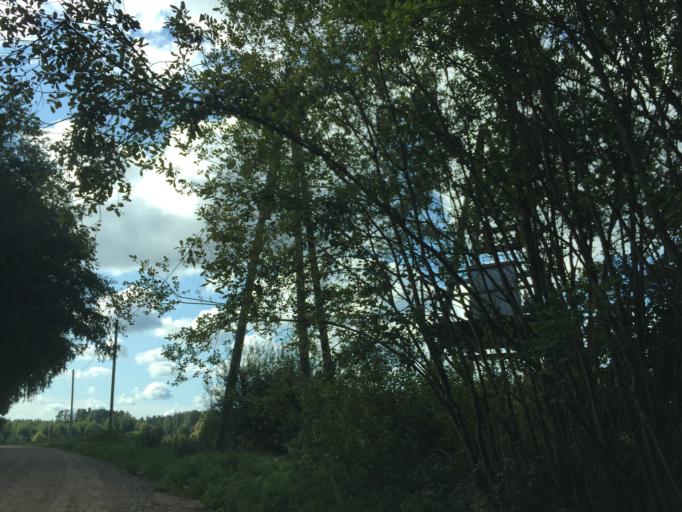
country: LV
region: Incukalns
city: Vangazi
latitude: 57.0884
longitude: 24.5633
